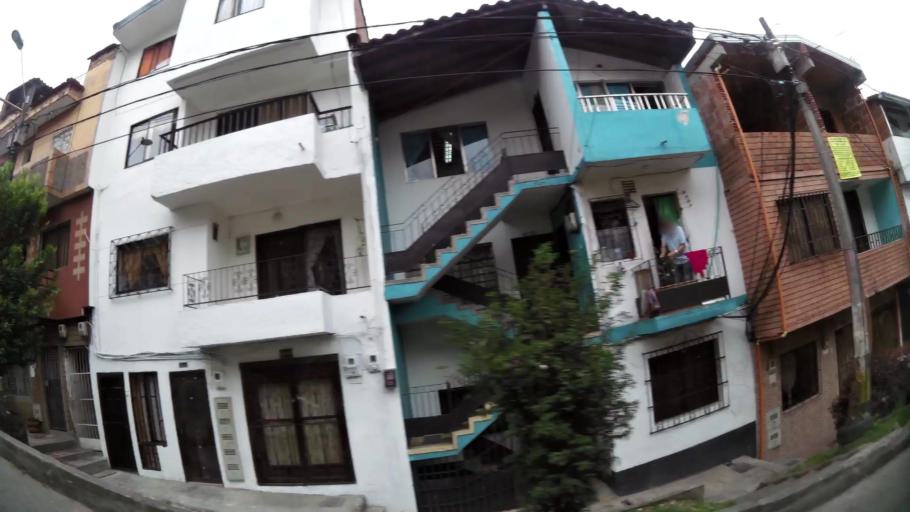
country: CO
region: Antioquia
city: Medellin
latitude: 6.2344
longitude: -75.5545
